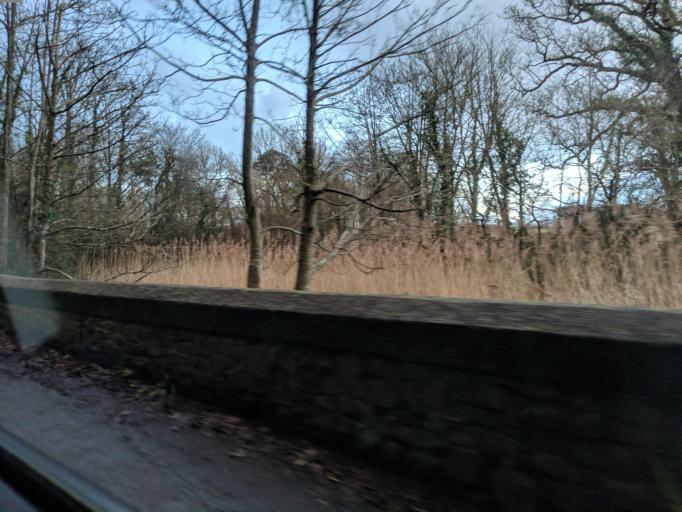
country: GB
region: England
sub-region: Devon
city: Fremington
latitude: 51.0731
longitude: -4.1110
